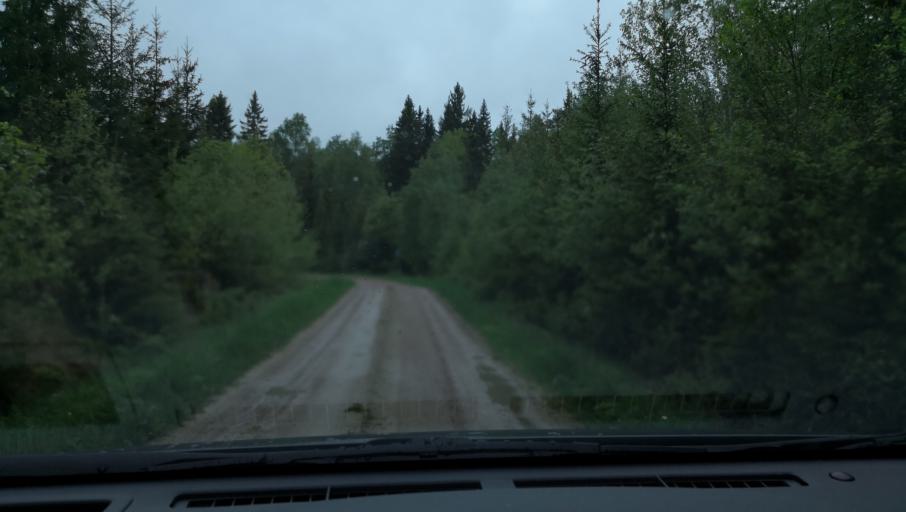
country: SE
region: Uppsala
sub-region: Enkopings Kommun
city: Orsundsbro
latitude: 59.9186
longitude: 17.3463
